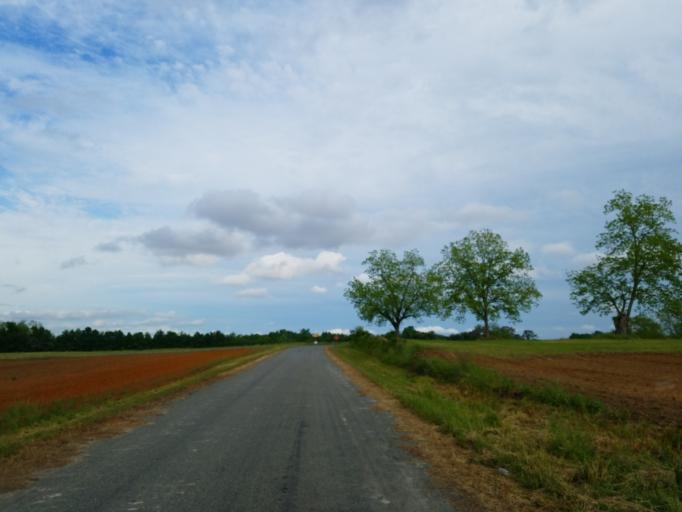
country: US
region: Georgia
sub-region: Dooly County
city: Unadilla
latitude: 32.1869
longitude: -83.7568
